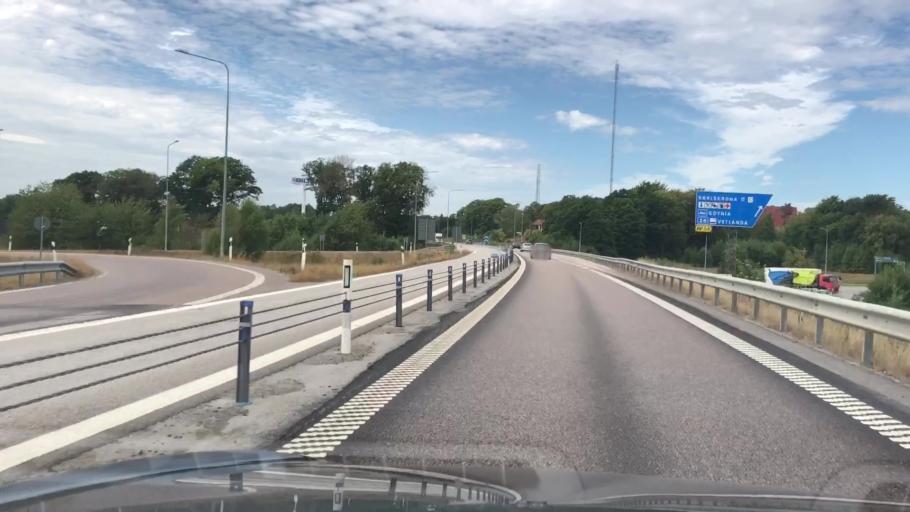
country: SE
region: Blekinge
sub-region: Karlskrona Kommun
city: Rodeby
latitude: 56.2057
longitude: 15.6444
